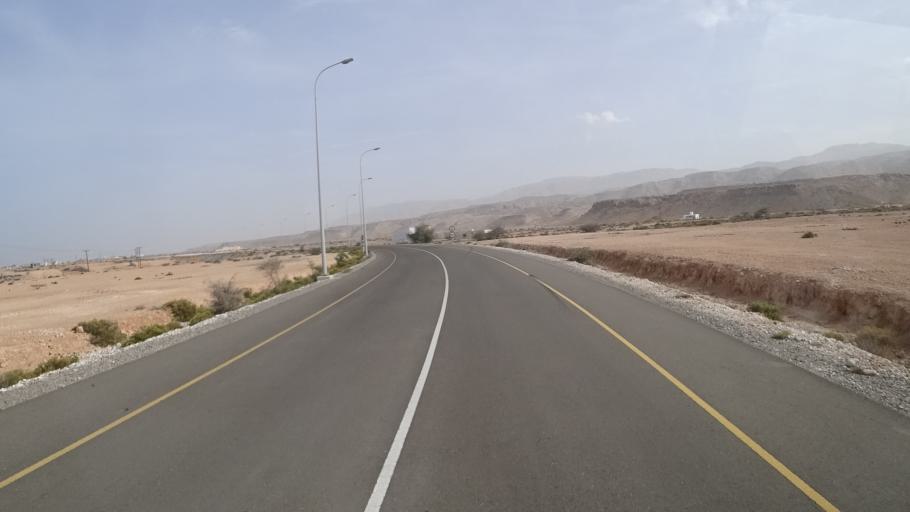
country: OM
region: Ash Sharqiyah
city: Sur
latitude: 23.0021
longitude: 59.1180
